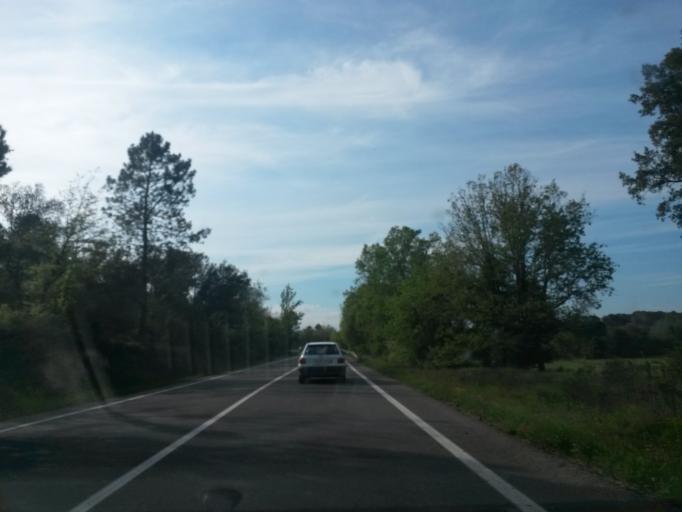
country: ES
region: Catalonia
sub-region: Provincia de Girona
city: Caldes de Malavella
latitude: 41.8419
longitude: 2.7885
